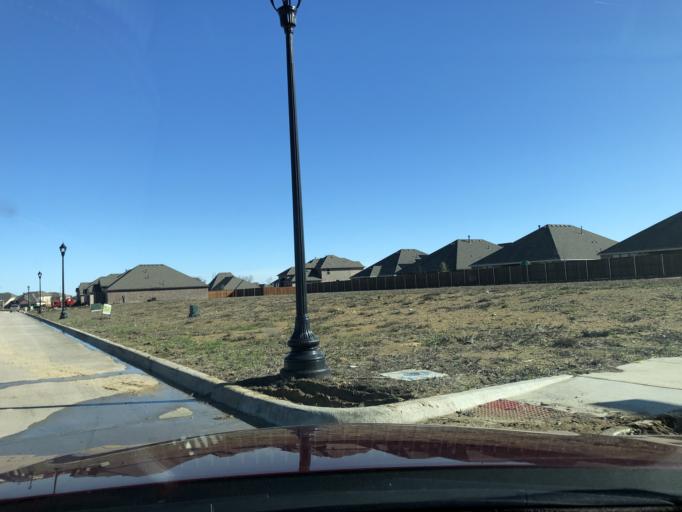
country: US
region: Texas
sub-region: Tarrant County
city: Haslet
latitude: 32.9489
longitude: -97.4007
